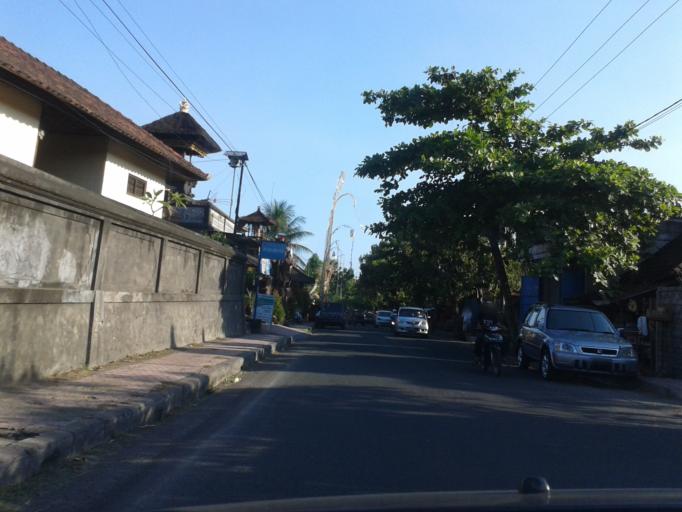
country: ID
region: Bali
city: Klungkung
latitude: -8.5186
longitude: 115.4010
